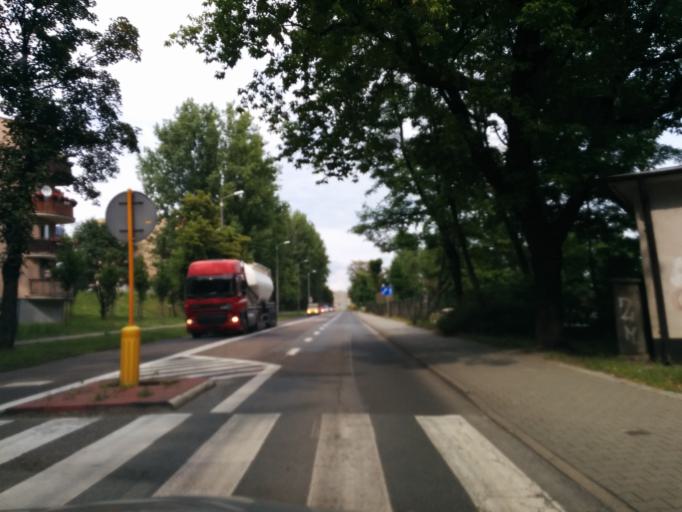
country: PL
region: Silesian Voivodeship
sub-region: Ruda Slaska
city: Ruda Slaska
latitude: 50.2760
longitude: 18.8528
